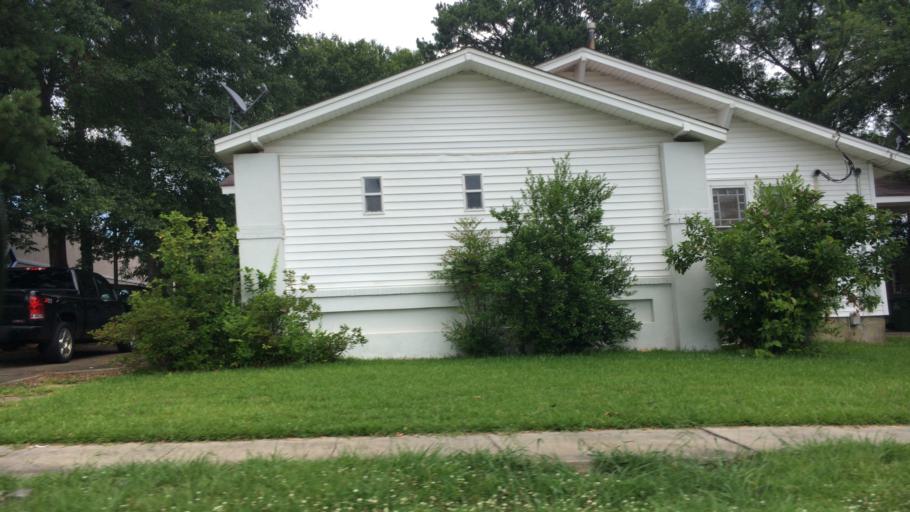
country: US
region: Louisiana
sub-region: Lincoln Parish
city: Ruston
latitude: 32.5231
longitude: -92.6397
